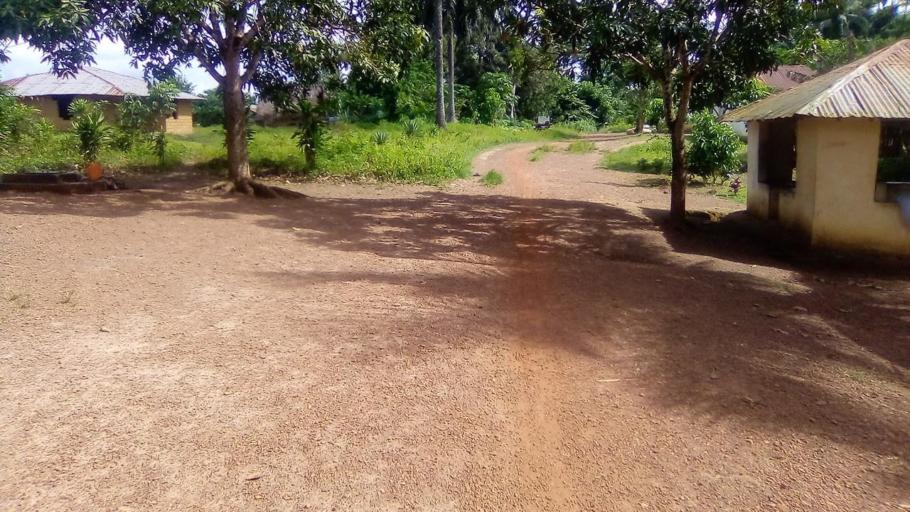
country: SL
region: Southern Province
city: Pujehun
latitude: 7.3742
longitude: -11.7284
